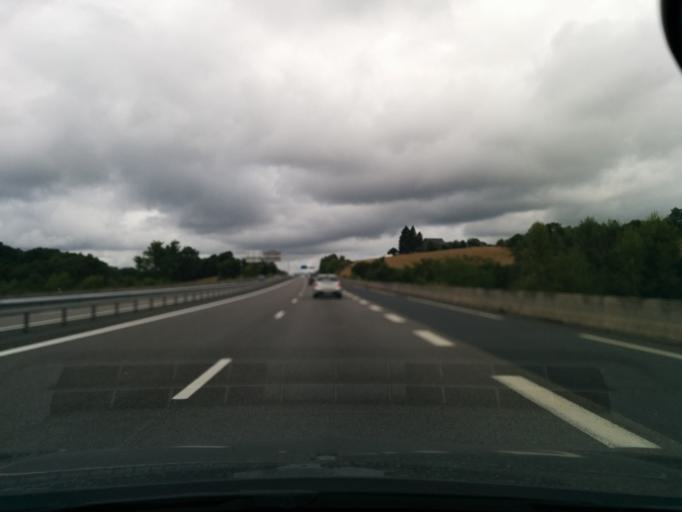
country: FR
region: Limousin
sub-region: Departement de la Correze
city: Saint-Mexant
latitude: 45.3127
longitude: 1.5755
